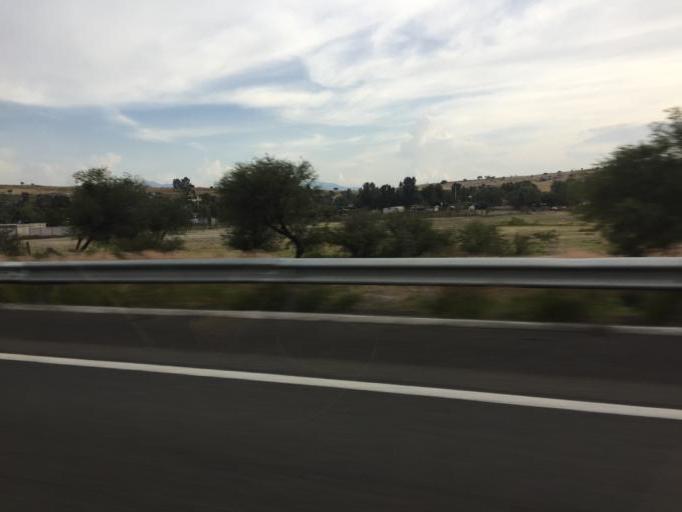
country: MX
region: Michoacan
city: Querendaro
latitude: 19.8873
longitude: -100.9526
